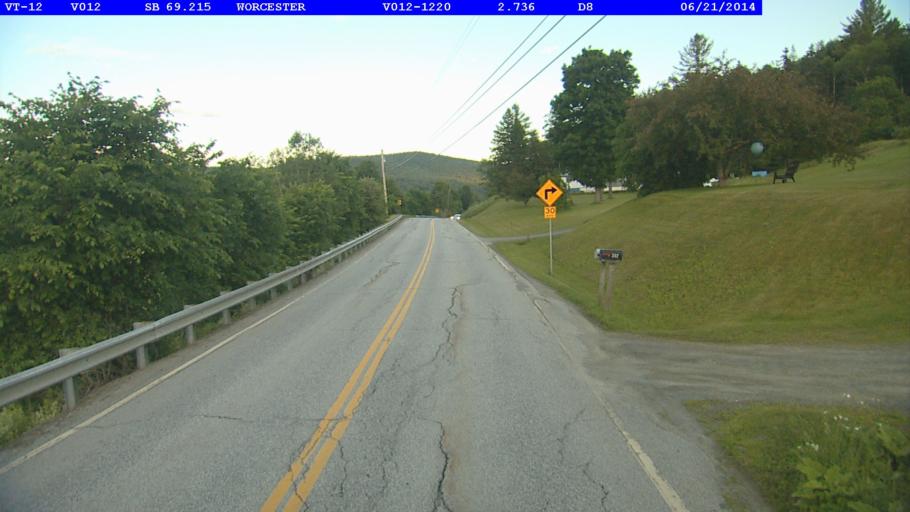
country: US
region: Vermont
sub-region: Washington County
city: Montpelier
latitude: 44.3871
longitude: -72.5548
